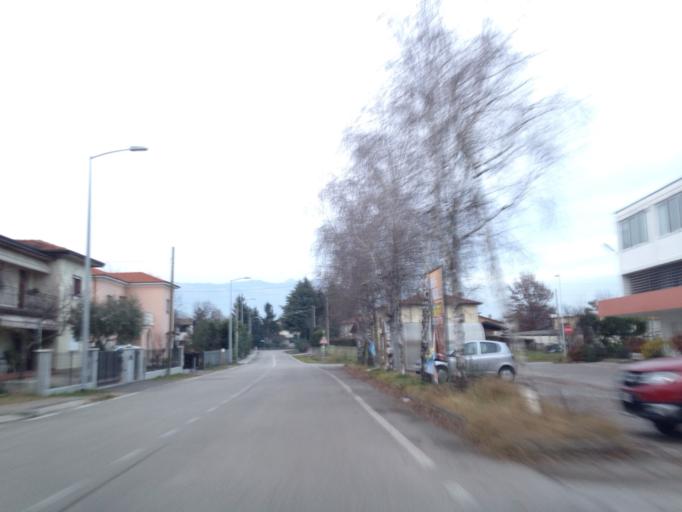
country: IT
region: Friuli Venezia Giulia
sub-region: Provincia di Pordenone
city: Cavolano-Schiavoi
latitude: 45.9424
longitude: 12.4937
